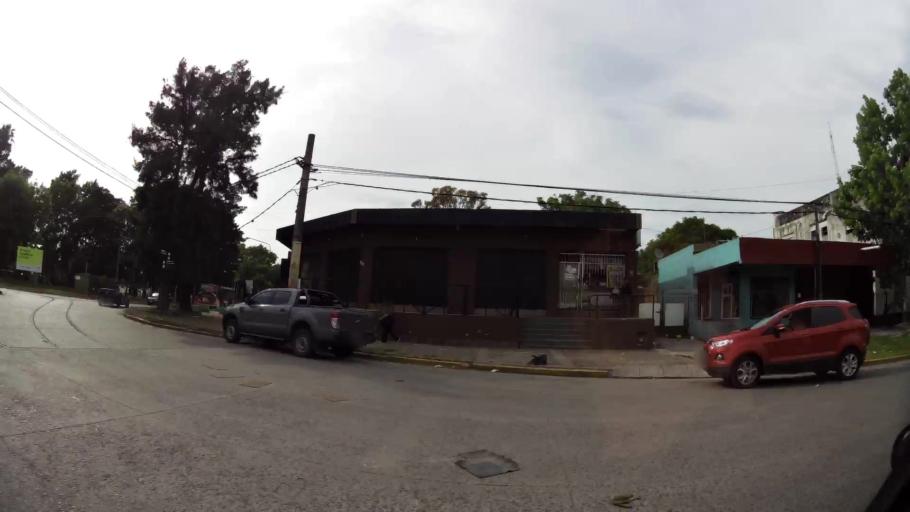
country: AR
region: Buenos Aires
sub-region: Partido de Quilmes
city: Quilmes
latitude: -34.7106
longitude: -58.2237
